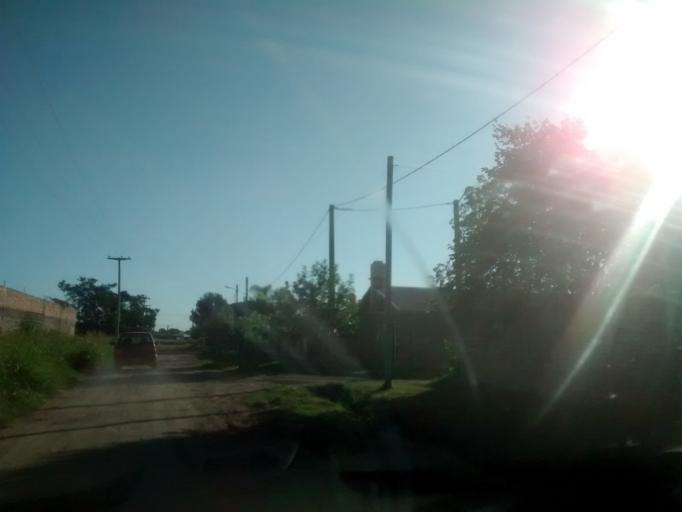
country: AR
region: Chaco
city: Fontana
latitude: -27.4606
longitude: -59.0358
